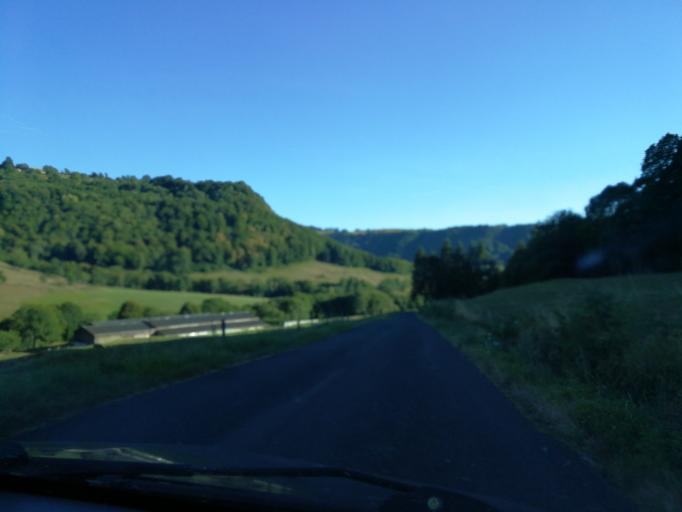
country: FR
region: Auvergne
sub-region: Departement du Cantal
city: Saint-Cernin
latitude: 45.1331
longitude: 2.4982
